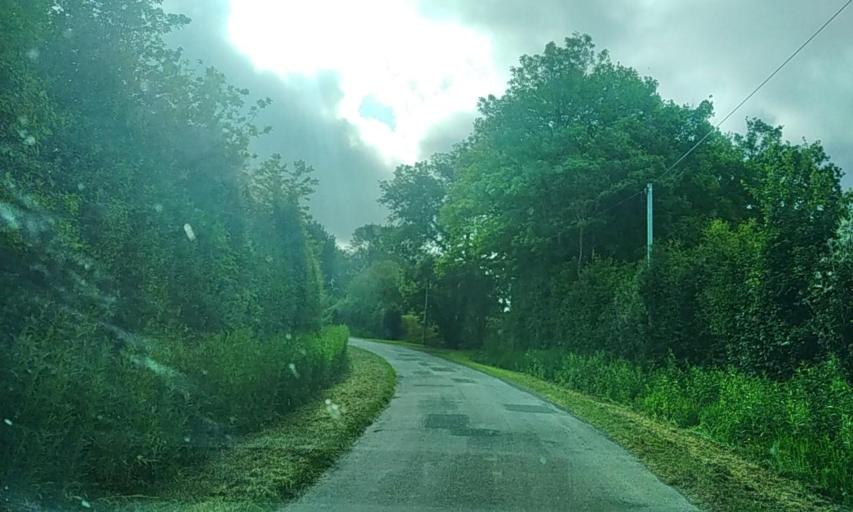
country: FR
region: Poitou-Charentes
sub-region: Departement des Deux-Sevres
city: Boisme
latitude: 46.7659
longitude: -0.4236
